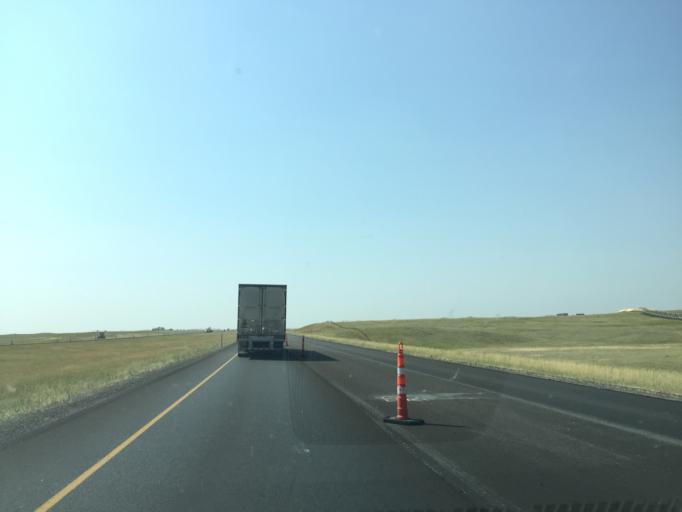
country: US
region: Wyoming
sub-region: Laramie County
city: Ranchettes
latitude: 41.3088
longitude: -104.8570
